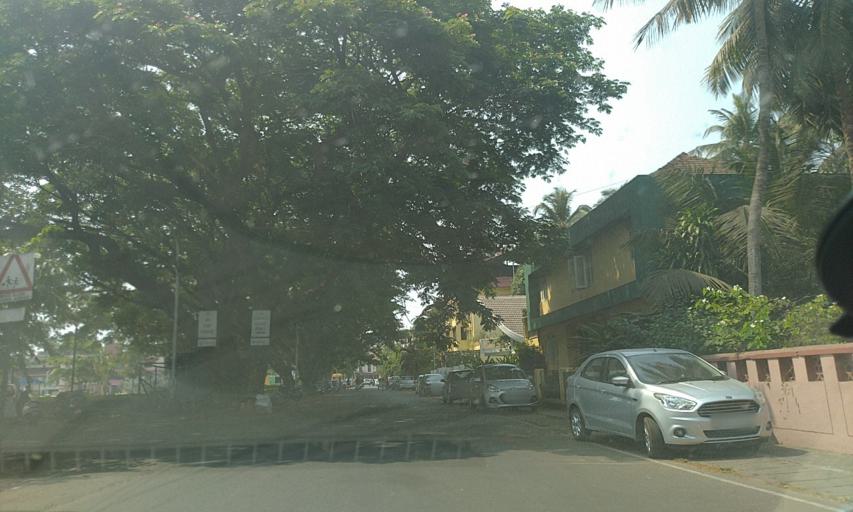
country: IN
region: Goa
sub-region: North Goa
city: Panaji
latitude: 15.4855
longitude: 73.8135
